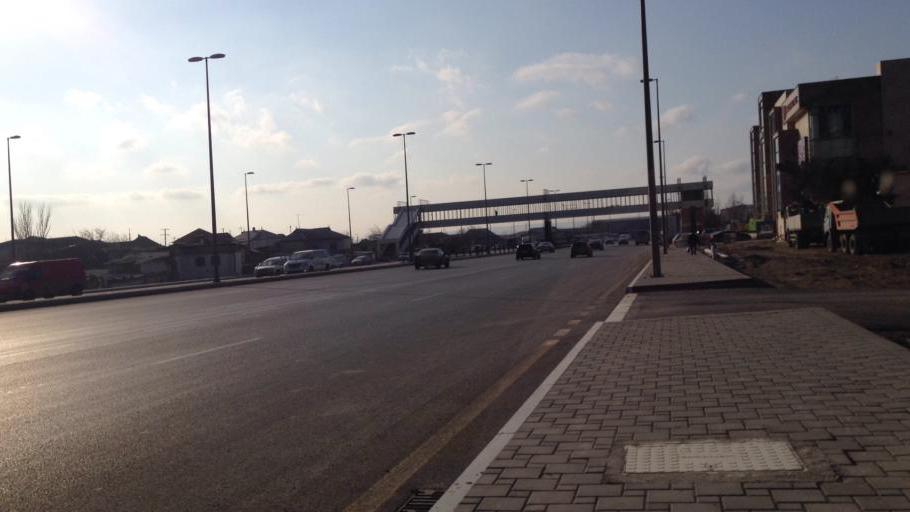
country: AZ
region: Baki
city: Balakhani
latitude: 40.4259
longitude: 49.9088
